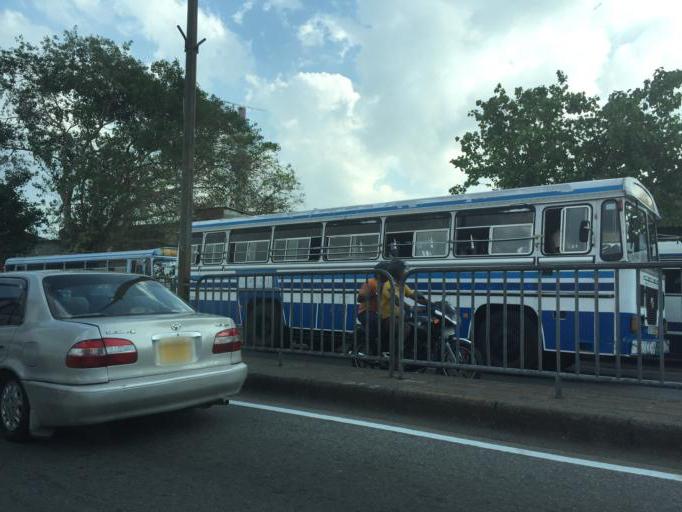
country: LK
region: Western
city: Colombo
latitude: 6.9345
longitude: 79.8547
